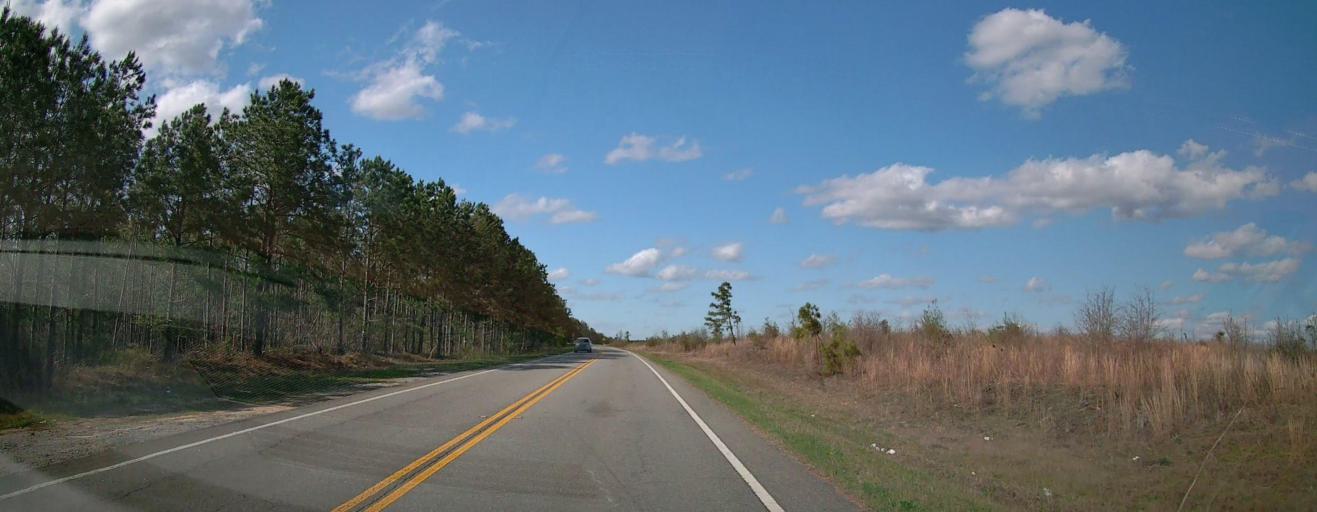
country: US
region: Georgia
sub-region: Wilkinson County
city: Gordon
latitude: 32.9439
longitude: -83.2898
